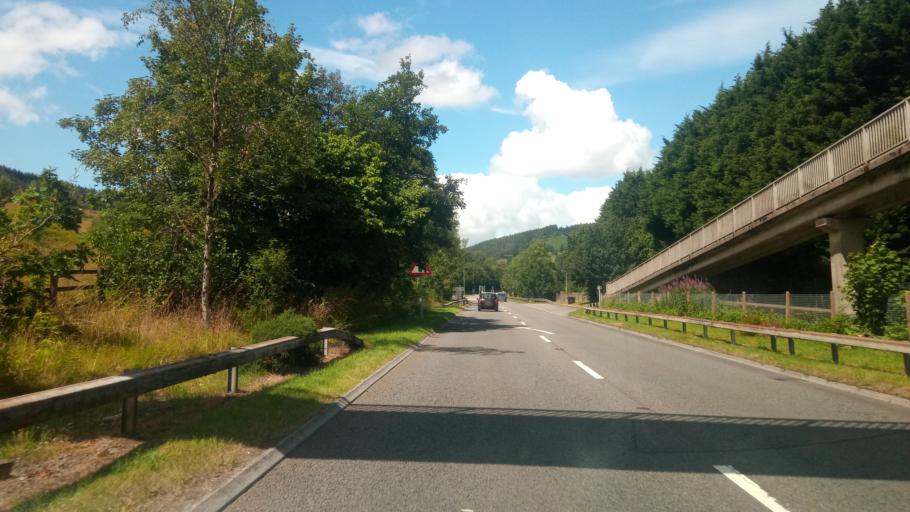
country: GB
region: Wales
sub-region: Rhondda Cynon Taf
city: Tonypandy
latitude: 51.6171
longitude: -3.4544
